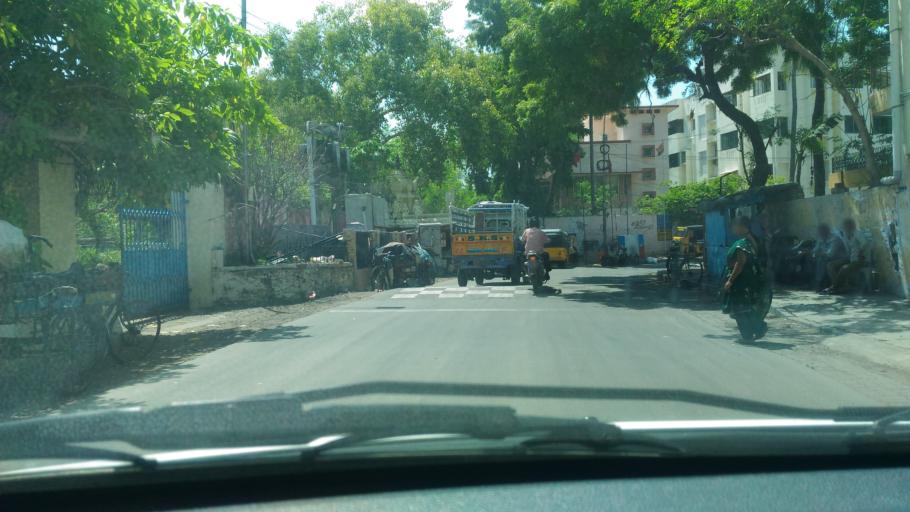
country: IN
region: Tamil Nadu
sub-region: Chennai
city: Chetput
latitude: 13.0511
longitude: 80.2453
